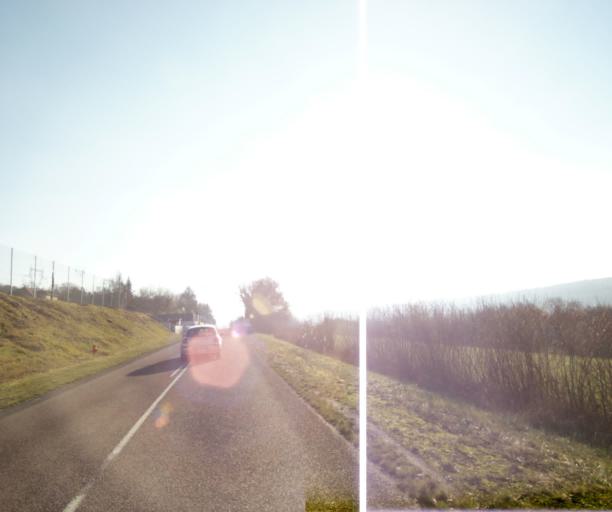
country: FR
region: Champagne-Ardenne
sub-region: Departement de la Haute-Marne
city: Chevillon
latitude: 48.5178
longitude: 5.1184
